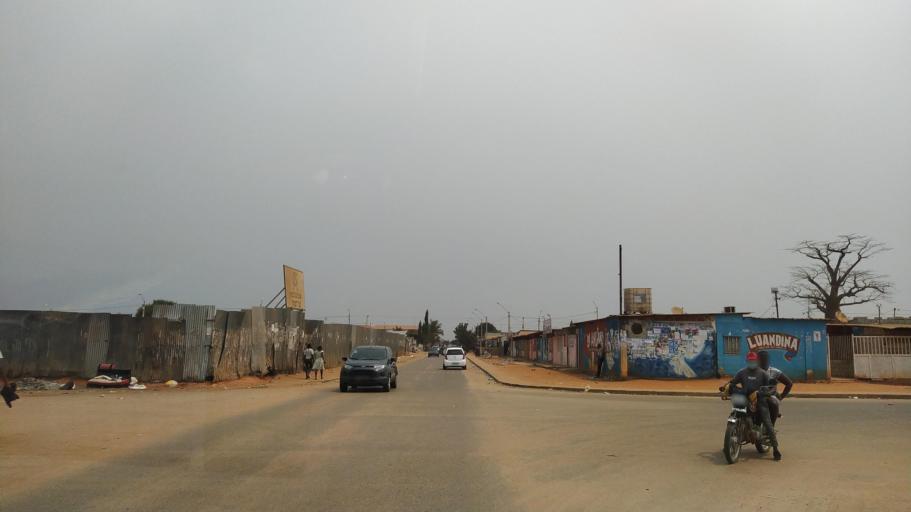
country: AO
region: Luanda
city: Luanda
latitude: -9.0712
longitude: 13.4115
